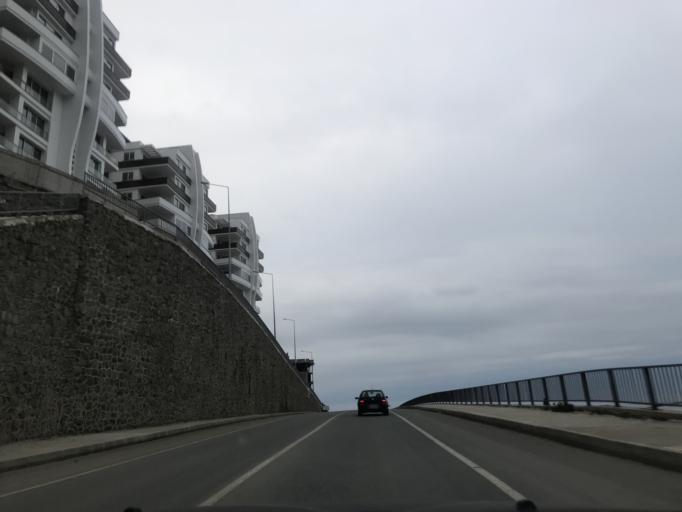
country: TR
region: Trabzon
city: Akcaabat
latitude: 41.0021
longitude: 39.6269
